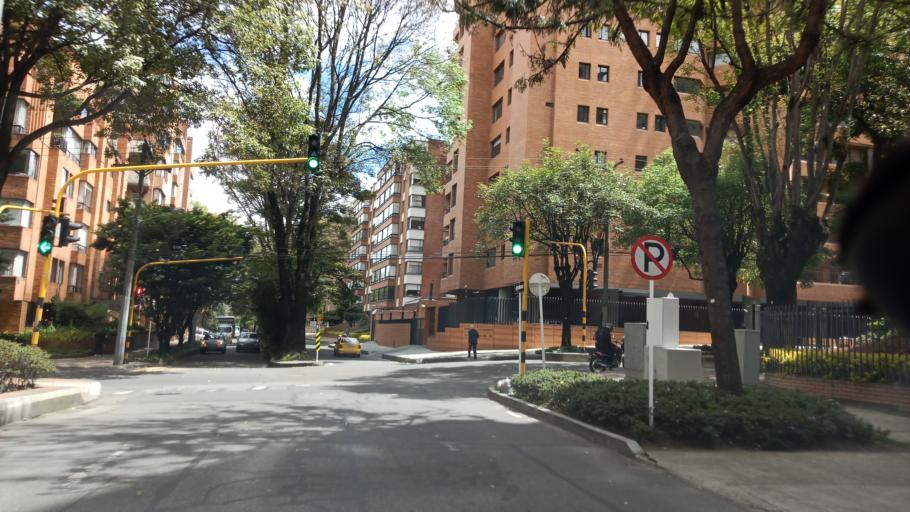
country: CO
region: Bogota D.C.
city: Barrio San Luis
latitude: 4.6662
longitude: -74.0493
